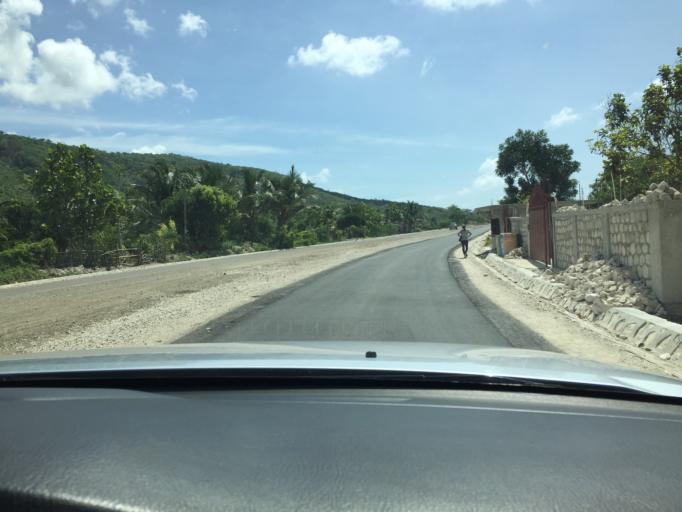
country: HT
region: Sud
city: Aquin
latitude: 18.2528
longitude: -73.3069
